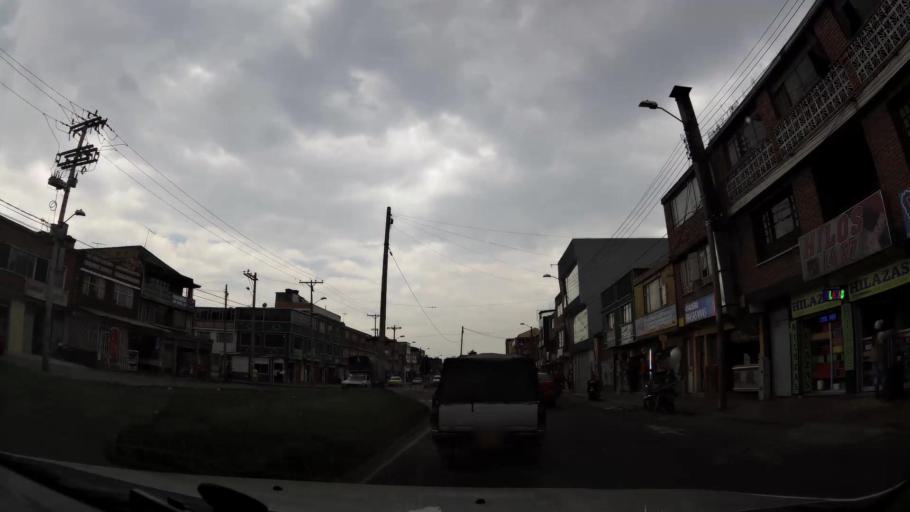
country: CO
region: Bogota D.C.
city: Bogota
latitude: 4.5772
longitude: -74.1044
